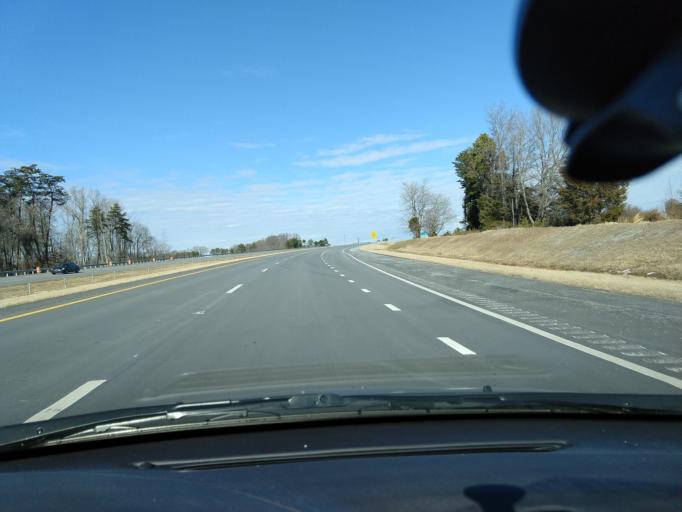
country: US
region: North Carolina
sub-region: Guilford County
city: Oak Ridge
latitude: 36.1298
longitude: -79.9657
